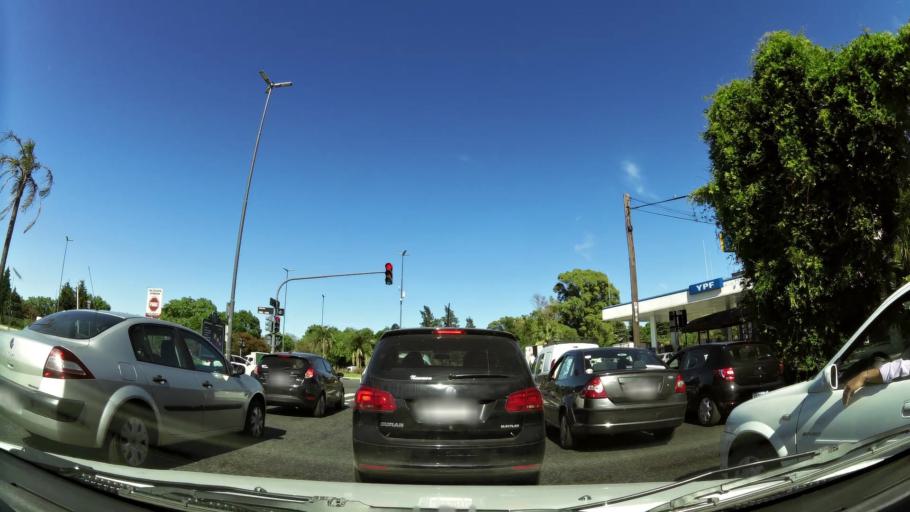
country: AR
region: Buenos Aires
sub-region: Partido de General San Martin
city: General San Martin
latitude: -34.5553
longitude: -58.4954
